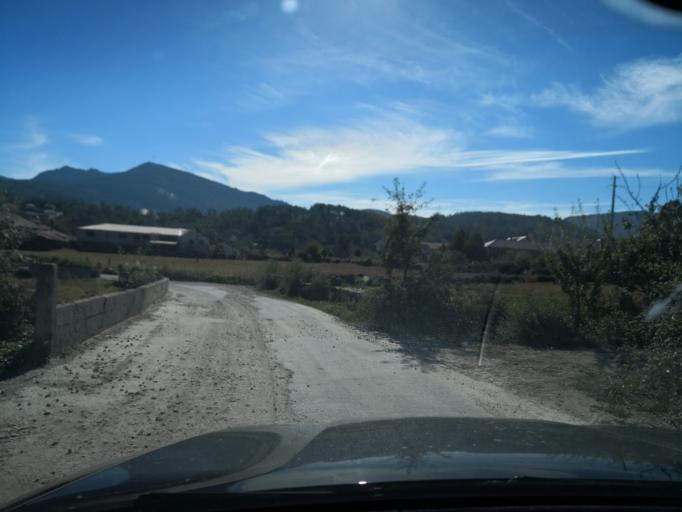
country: PT
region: Vila Real
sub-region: Santa Marta de Penaguiao
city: Santa Marta de Penaguiao
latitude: 41.3003
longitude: -7.8755
